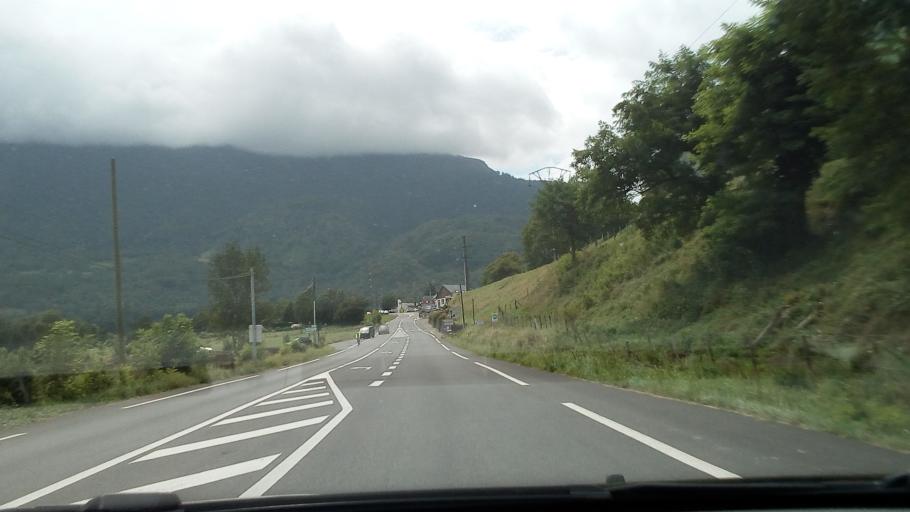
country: FR
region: Aquitaine
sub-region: Departement des Pyrenees-Atlantiques
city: Laruns
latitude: 42.9951
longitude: -0.4221
